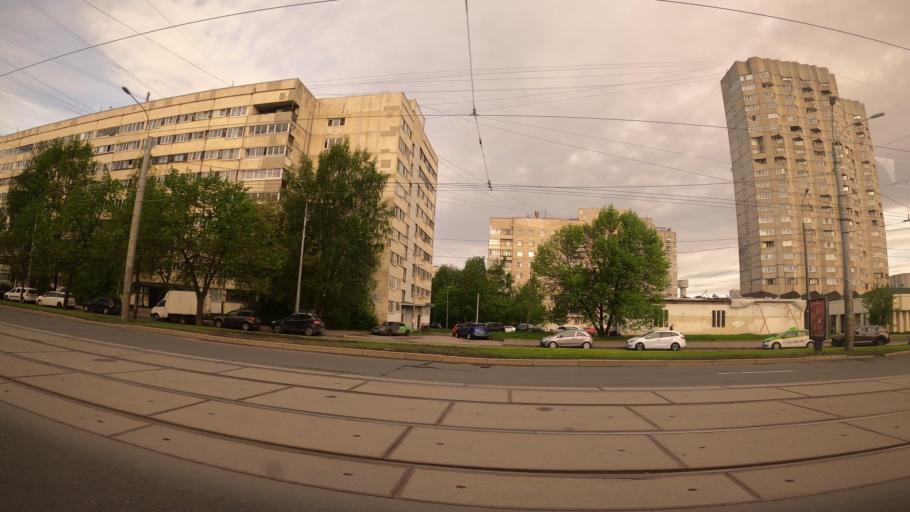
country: RU
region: St.-Petersburg
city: Vasyl'evsky Ostrov
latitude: 59.9462
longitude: 30.2306
